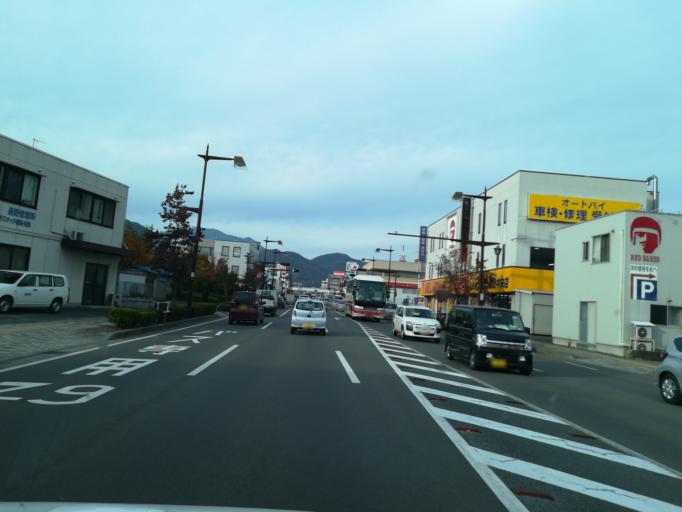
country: JP
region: Nagano
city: Nagano-shi
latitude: 36.6297
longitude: 138.1831
